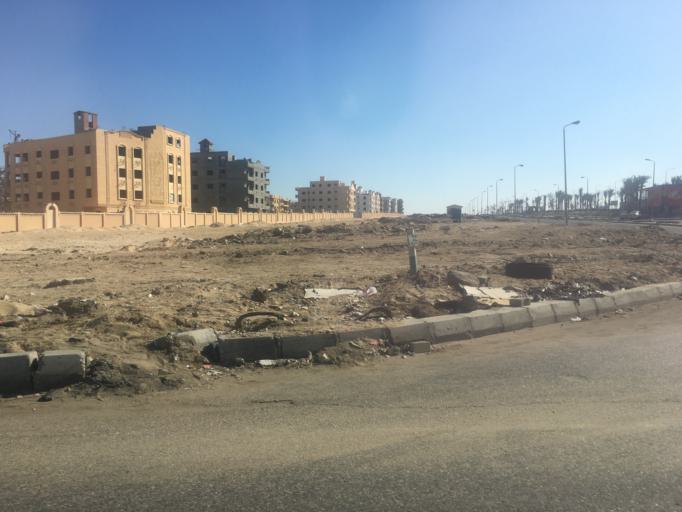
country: EG
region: Al Jizah
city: Awsim
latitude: 30.0166
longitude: 30.9762
